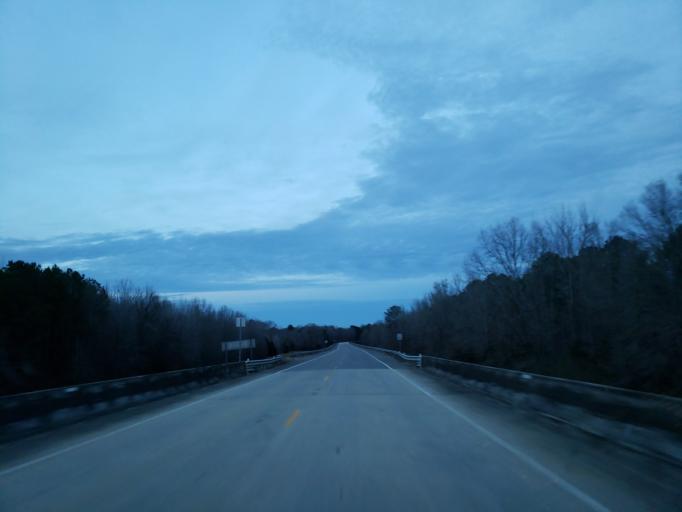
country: US
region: Alabama
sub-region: Sumter County
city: Livingston
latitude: 32.8268
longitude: -88.1552
